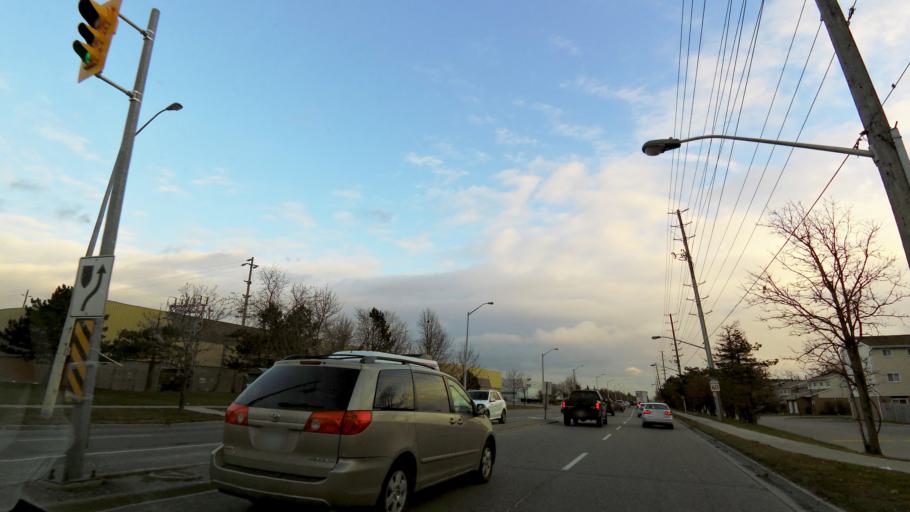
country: CA
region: Ontario
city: Brampton
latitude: 43.7273
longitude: -79.6977
